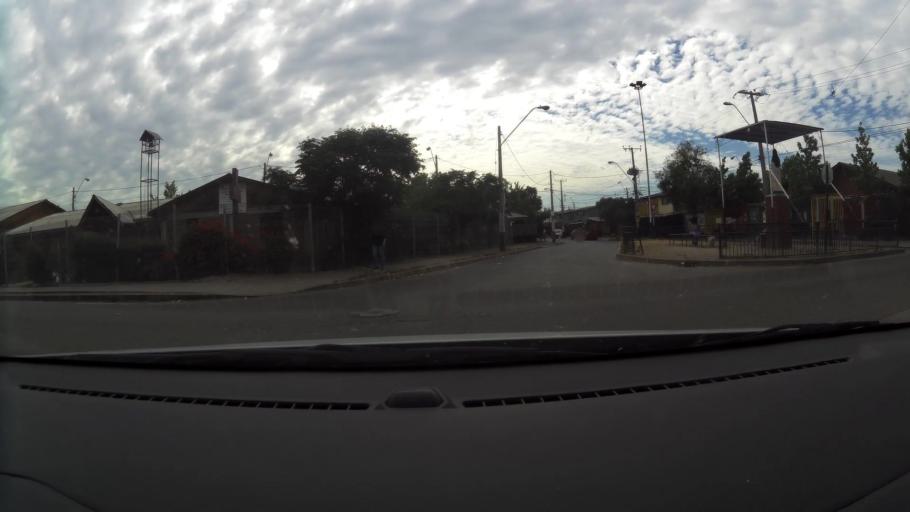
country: CL
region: Santiago Metropolitan
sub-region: Provincia de Santiago
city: La Pintana
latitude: -33.6133
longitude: -70.6225
